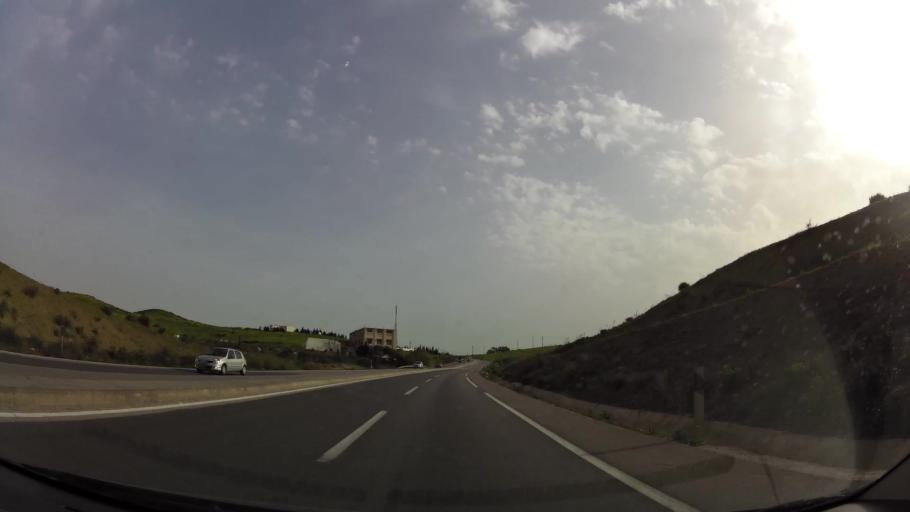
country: MA
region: Tanger-Tetouan
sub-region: Tanger-Assilah
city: Dar Chaoui
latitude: 35.6664
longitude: -5.6976
